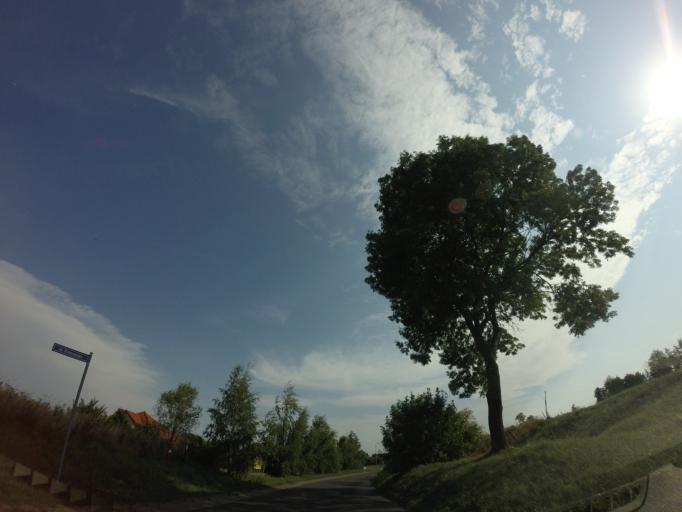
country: PL
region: West Pomeranian Voivodeship
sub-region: Powiat stargardzki
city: Stargard Szczecinski
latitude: 53.3011
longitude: 15.0495
